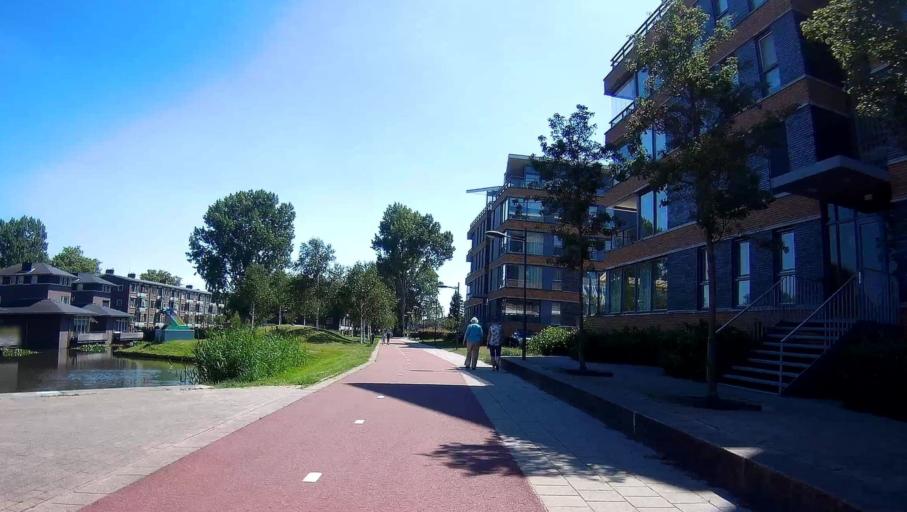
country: NL
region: South Holland
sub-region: Gemeente Westland
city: Naaldwijk
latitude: 51.9989
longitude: 4.2020
